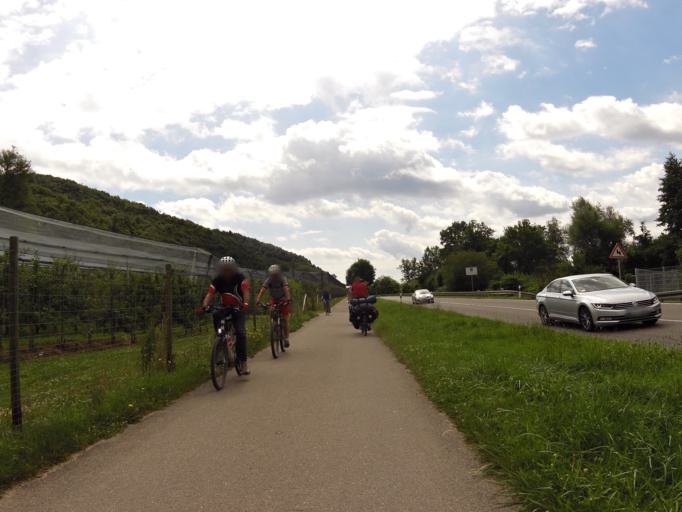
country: DE
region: Baden-Wuerttemberg
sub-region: Freiburg Region
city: Bodman-Ludwigshafen
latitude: 47.8081
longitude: 9.0709
